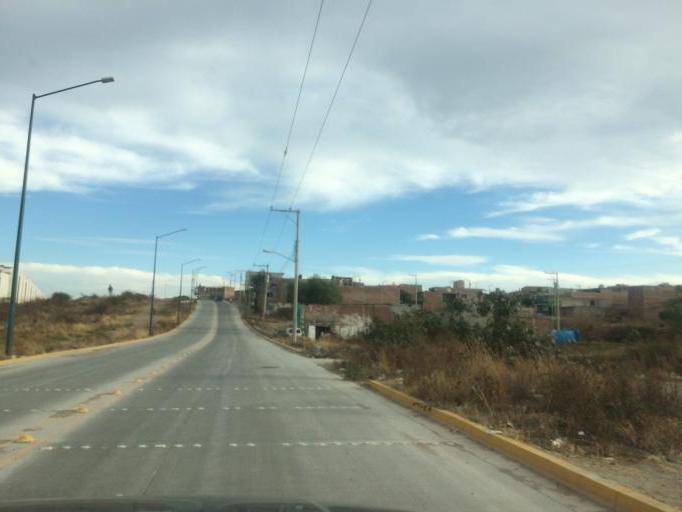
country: MX
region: Guanajuato
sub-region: Leon
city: Rizos de la Joya (Rizos del Saucillo)
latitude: 21.1457
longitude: -101.7549
